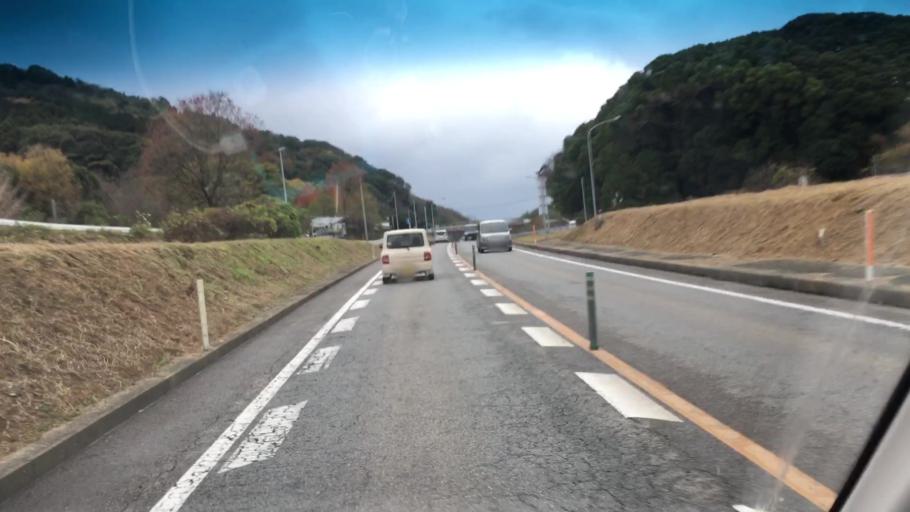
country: JP
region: Fukuoka
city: Maebaru-chuo
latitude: 33.5107
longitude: 130.1320
